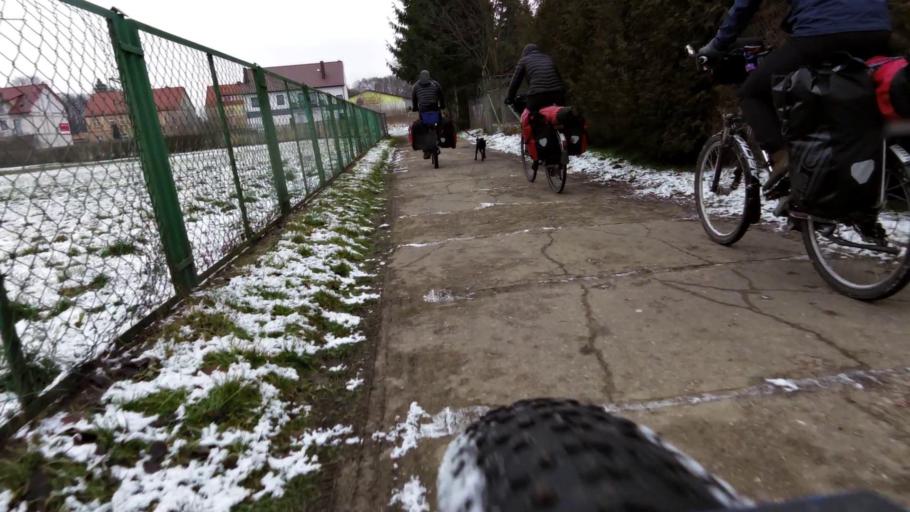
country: PL
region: West Pomeranian Voivodeship
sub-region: Powiat walecki
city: Miroslawiec
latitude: 53.3412
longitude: 16.0916
